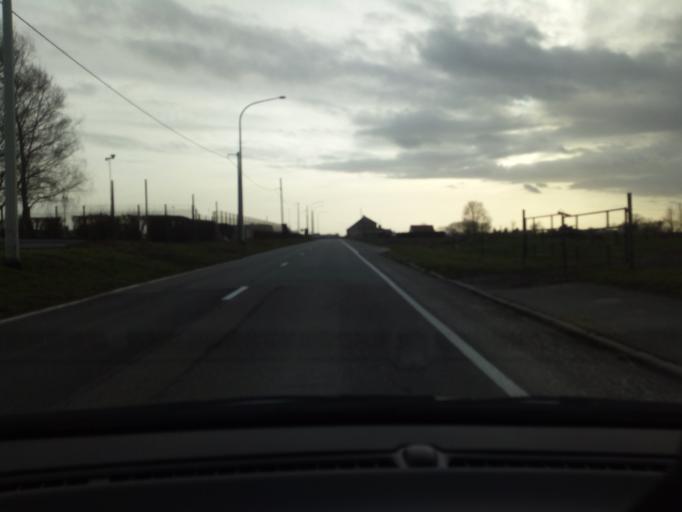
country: FR
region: Nord-Pas-de-Calais
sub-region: Departement du Nord
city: La Longueville
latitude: 50.3387
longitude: 3.8746
